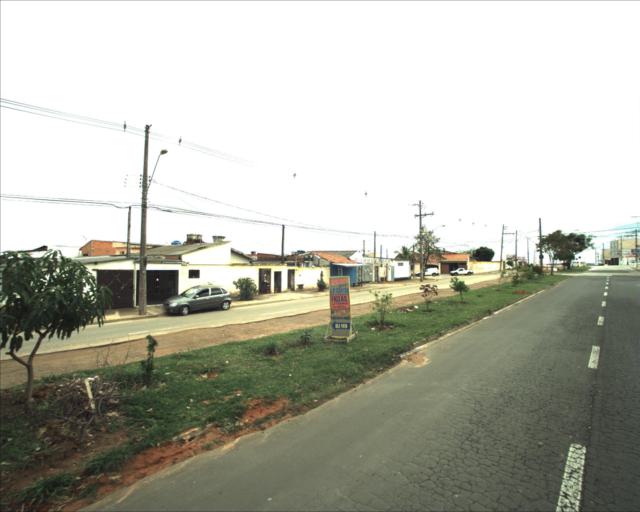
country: BR
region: Sao Paulo
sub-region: Sorocaba
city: Sorocaba
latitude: -23.4268
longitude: -47.4675
